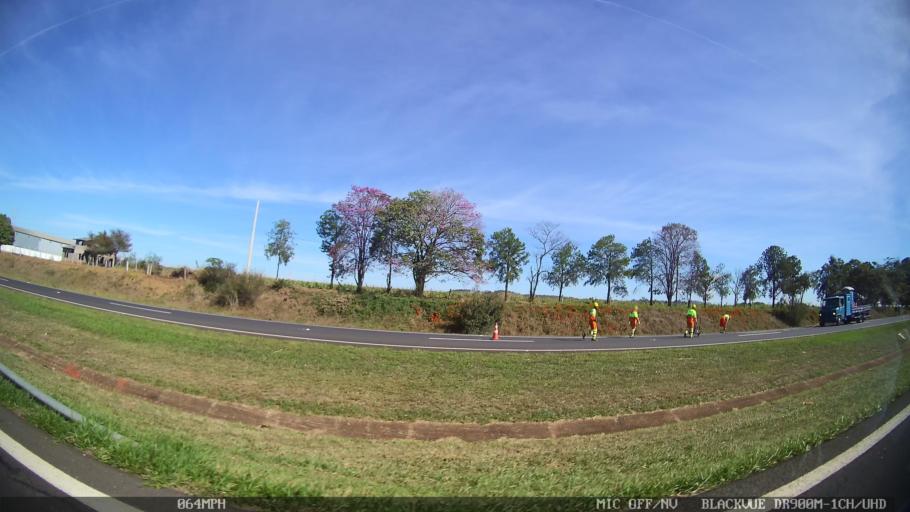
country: BR
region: Sao Paulo
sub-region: Pirassununga
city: Pirassununga
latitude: -22.0206
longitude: -47.4379
